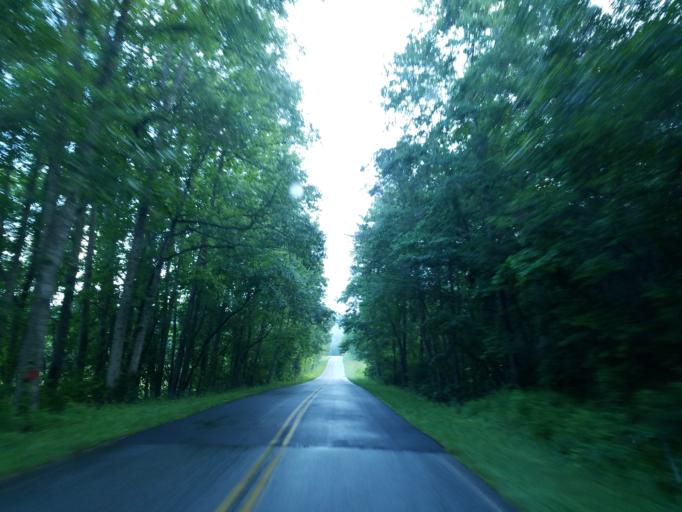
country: US
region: Georgia
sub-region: Fannin County
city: Blue Ridge
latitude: 34.7340
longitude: -84.2349
